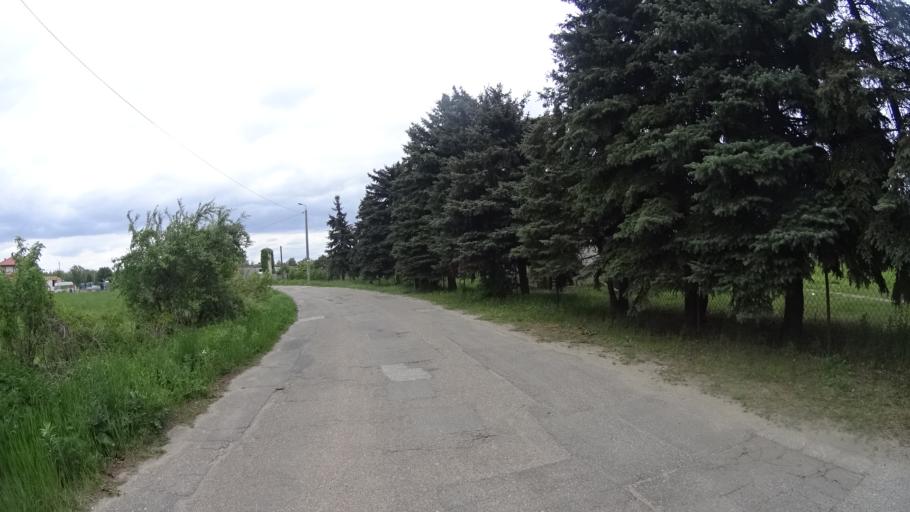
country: PL
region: Masovian Voivodeship
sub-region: Warszawa
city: Ursus
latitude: 52.2082
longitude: 20.8593
